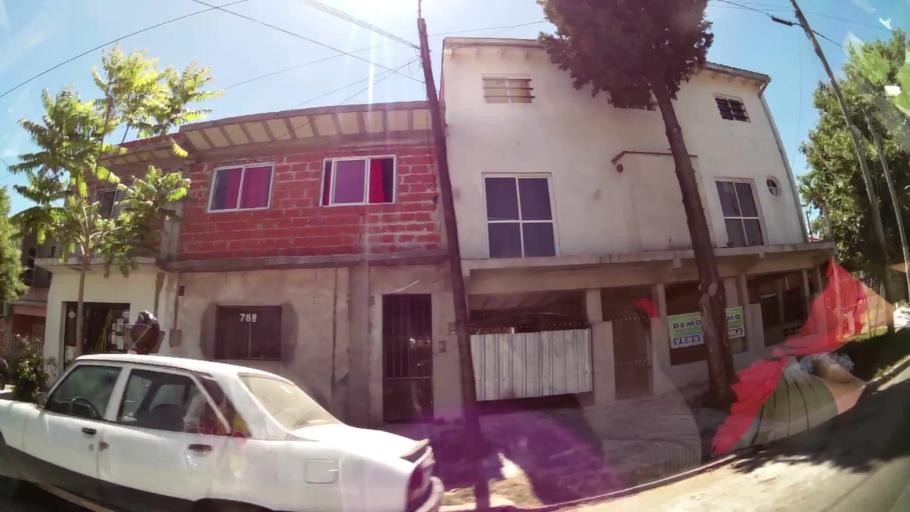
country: AR
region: Buenos Aires
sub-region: Partido de Tigre
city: Tigre
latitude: -34.4869
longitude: -58.6347
